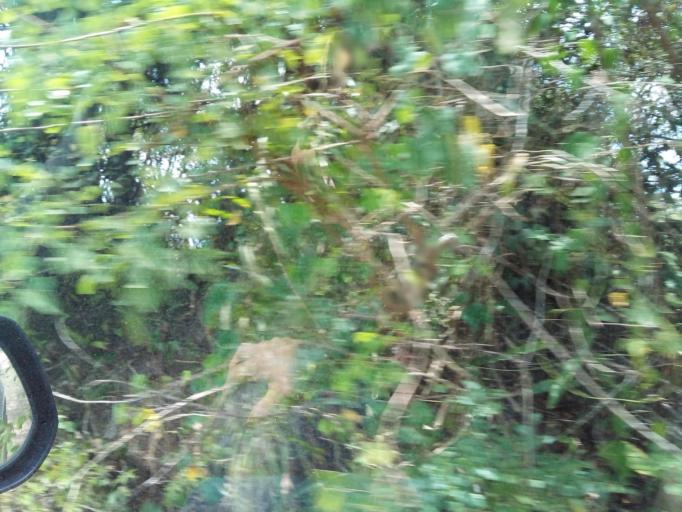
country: BR
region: Maranhao
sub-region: Itapecuru Mirim
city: Itapecuru Mirim
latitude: -3.1339
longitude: -44.3359
